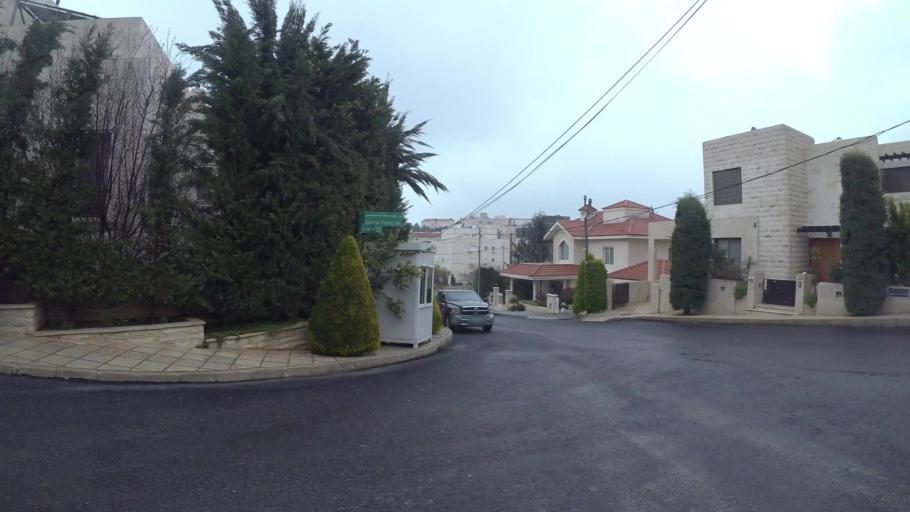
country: JO
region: Amman
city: Al Jubayhah
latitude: 32.0074
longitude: 35.8223
